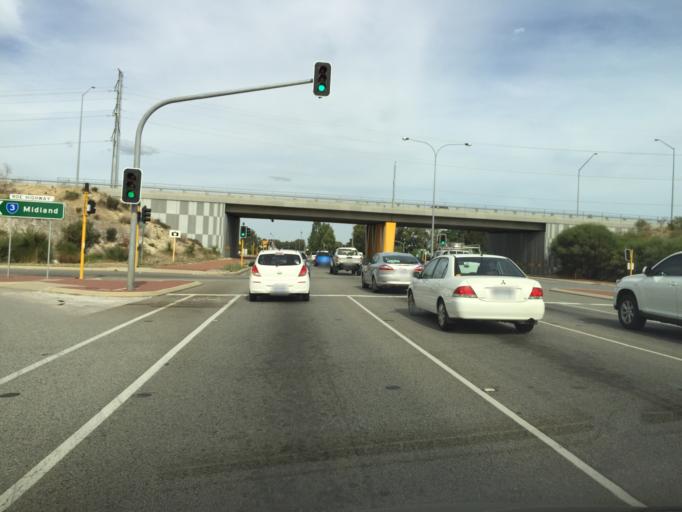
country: AU
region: Western Australia
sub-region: Canning
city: Willetton
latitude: -32.0687
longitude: 115.8892
